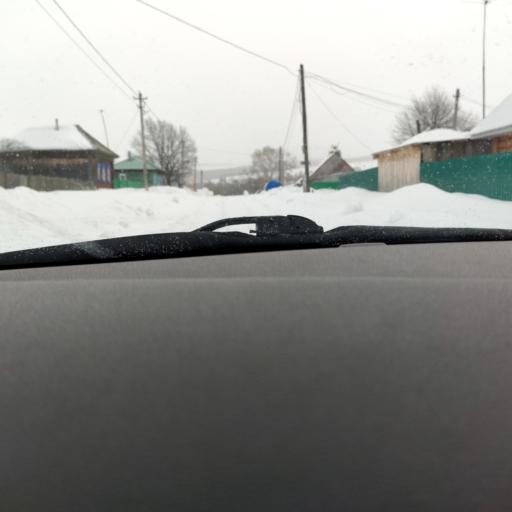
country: RU
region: Bashkortostan
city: Blagoveshchensk
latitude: 55.1728
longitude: 55.8355
